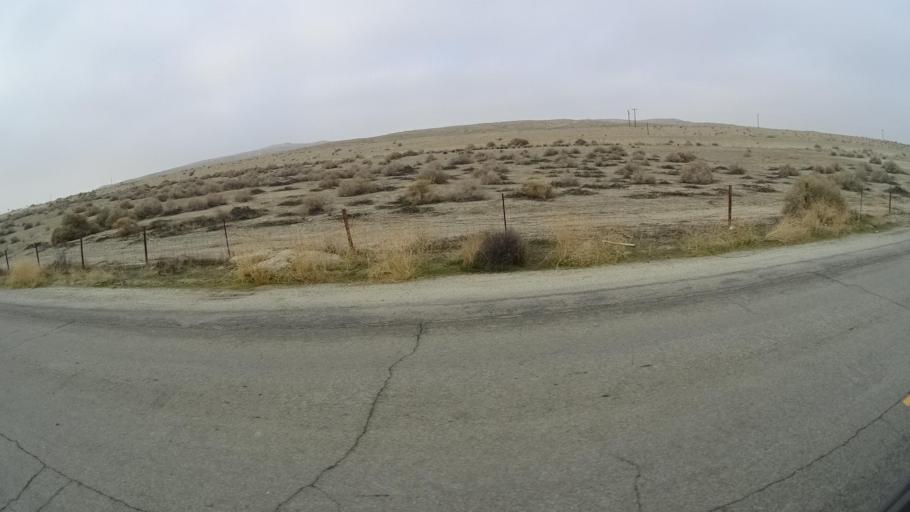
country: US
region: California
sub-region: Kern County
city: Maricopa
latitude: 35.1296
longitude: -119.3655
